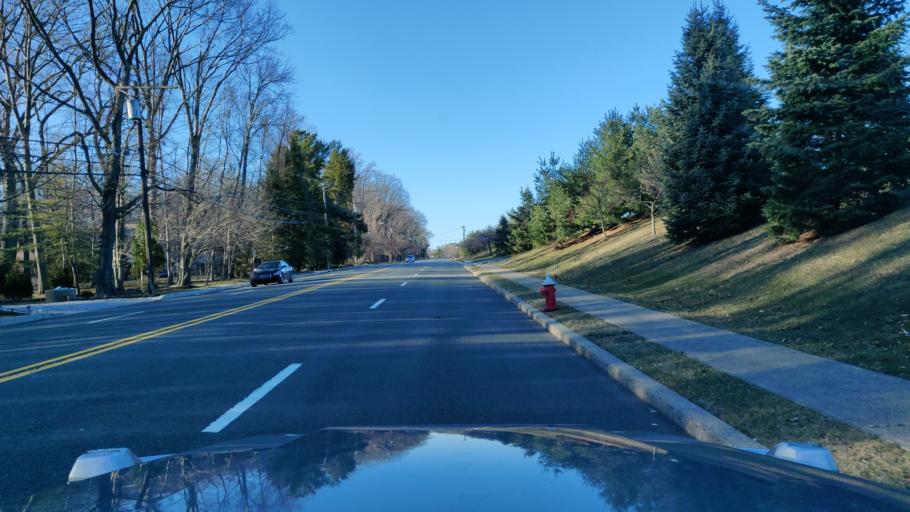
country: US
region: New Jersey
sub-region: Bergen County
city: Woodcliff Lake
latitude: 41.0282
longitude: -74.0742
